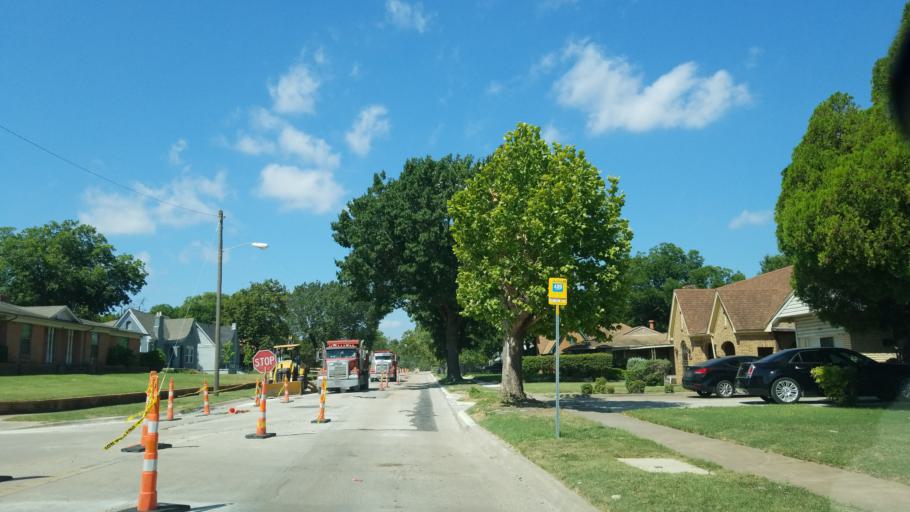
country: US
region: Texas
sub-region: Dallas County
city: Dallas
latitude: 32.7309
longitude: -96.7951
